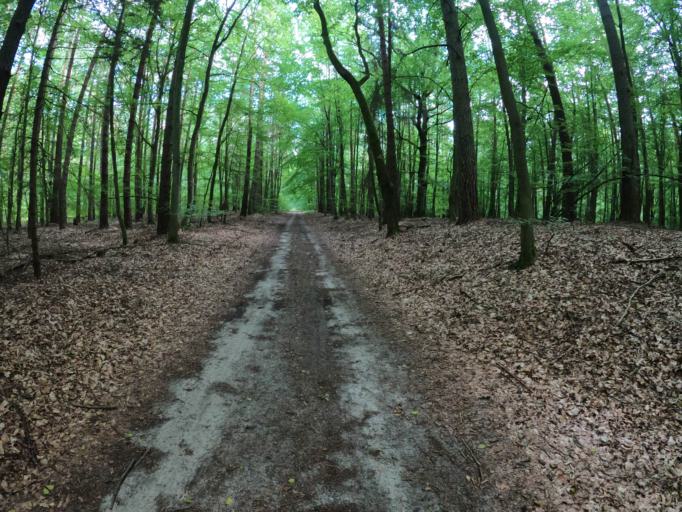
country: DE
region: Brandenburg
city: Angermunde
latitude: 53.0324
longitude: 13.9296
